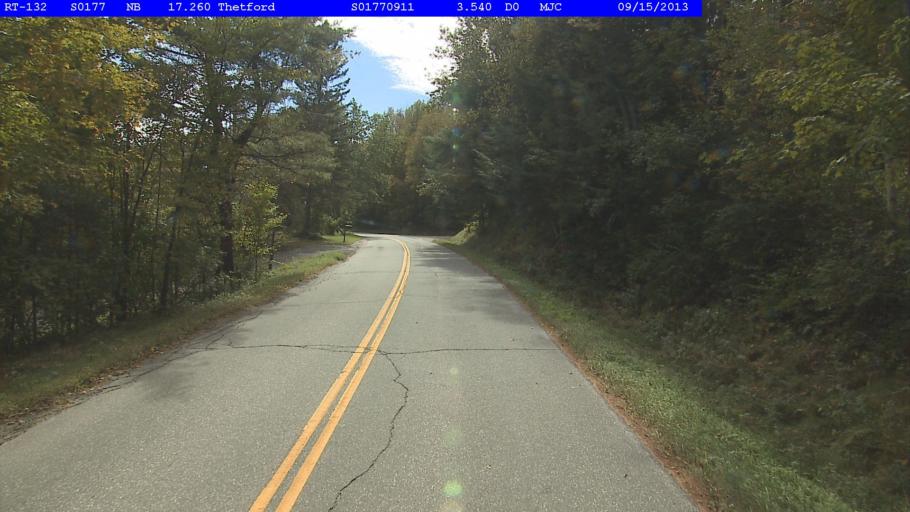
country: US
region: New Hampshire
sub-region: Grafton County
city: Hanover
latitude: 43.8078
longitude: -72.2713
